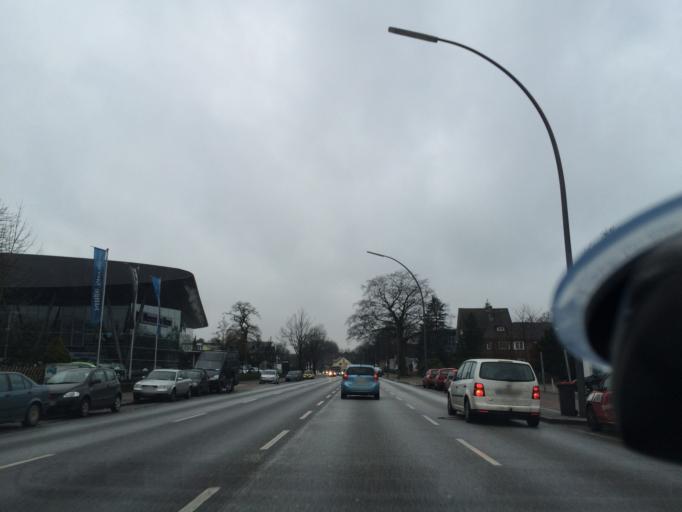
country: DE
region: Schleswig-Holstein
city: Halstenbek
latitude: 53.5724
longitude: 9.8514
